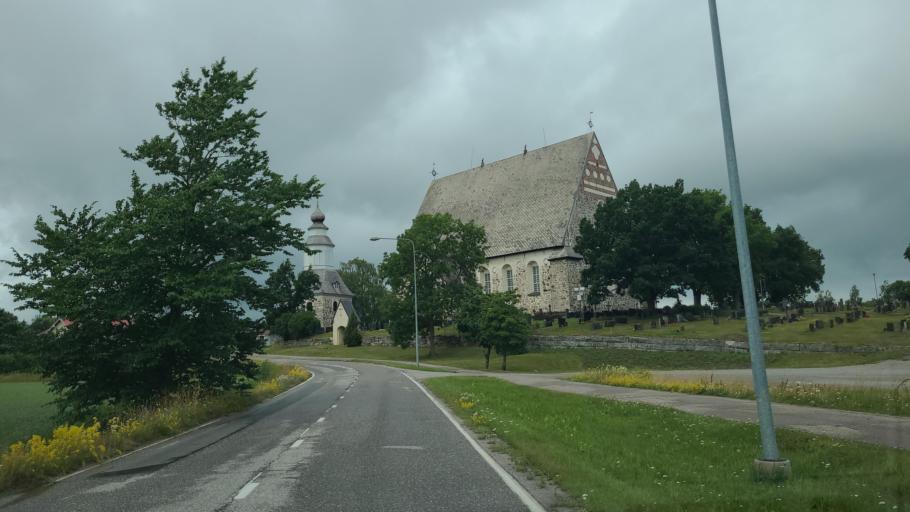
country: FI
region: Varsinais-Suomi
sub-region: Turku
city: Sauvo
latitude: 60.3419
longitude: 22.7007
